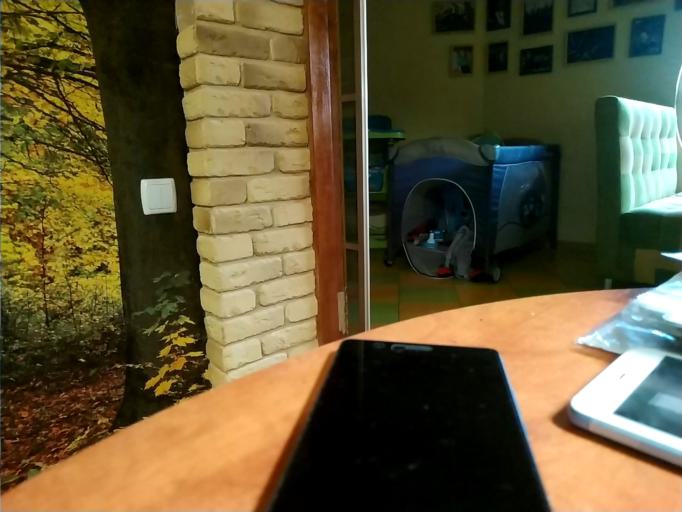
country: RU
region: Orjol
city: Znamenskoye
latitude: 53.6066
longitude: 35.4669
